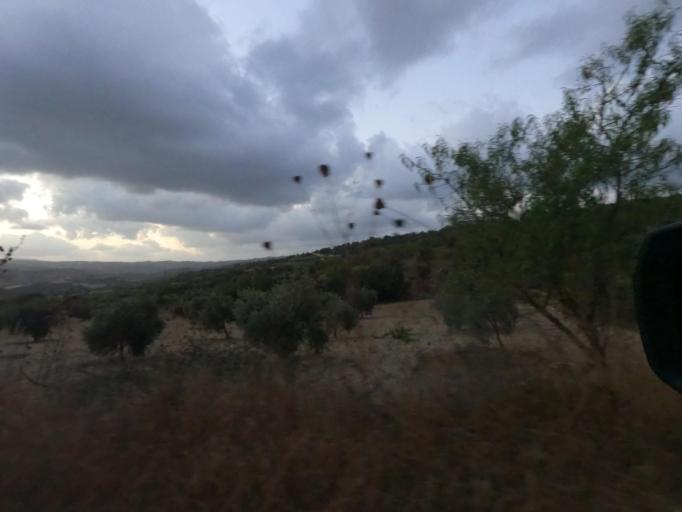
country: CY
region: Pafos
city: Mesogi
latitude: 34.8511
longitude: 32.5294
